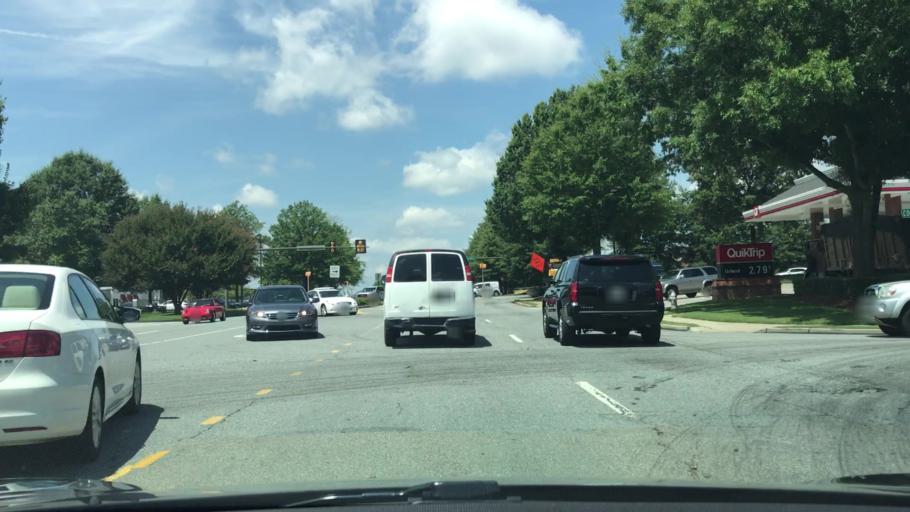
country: US
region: Georgia
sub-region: Fulton County
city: Johns Creek
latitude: 34.0718
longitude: -84.1654
